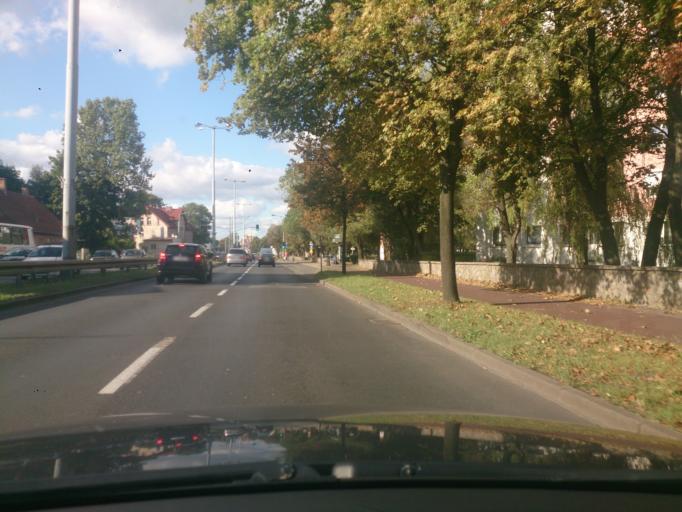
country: PL
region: Pomeranian Voivodeship
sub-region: Sopot
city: Sopot
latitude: 54.4194
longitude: 18.5653
